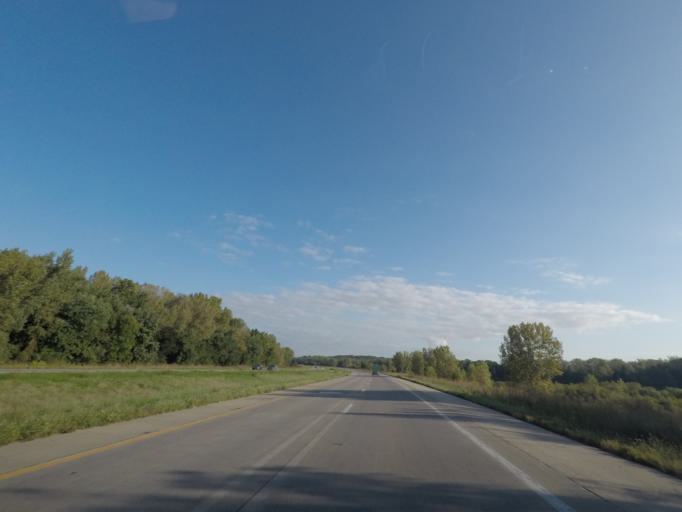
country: US
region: Iowa
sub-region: Polk County
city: Pleasant Hill
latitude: 41.5534
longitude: -93.5109
